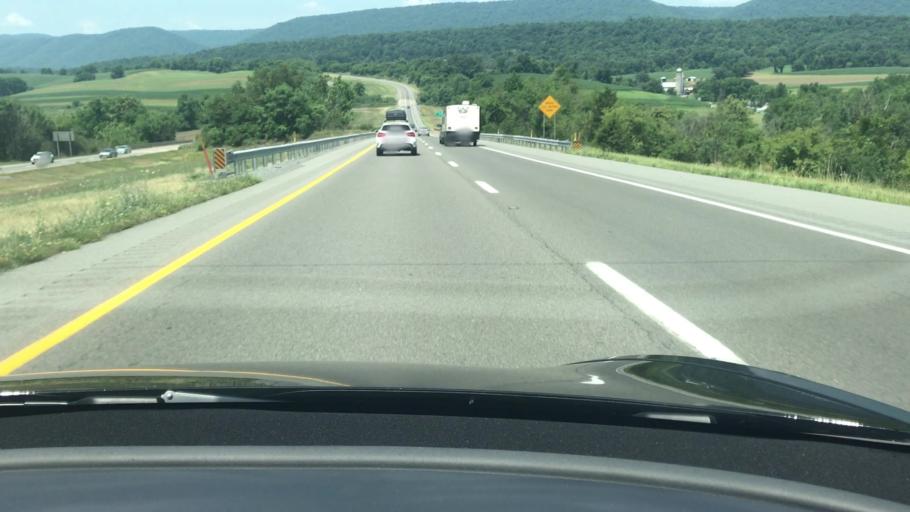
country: US
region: Pennsylvania
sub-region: Juniata County
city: Mifflintown
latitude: 40.5999
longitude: -77.3874
